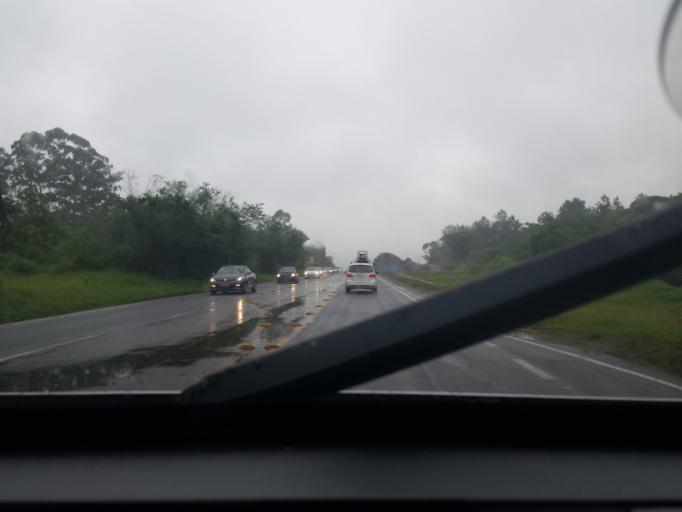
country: BR
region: Santa Catarina
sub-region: Navegantes
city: Navegantes
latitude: -26.8336
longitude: -48.7367
